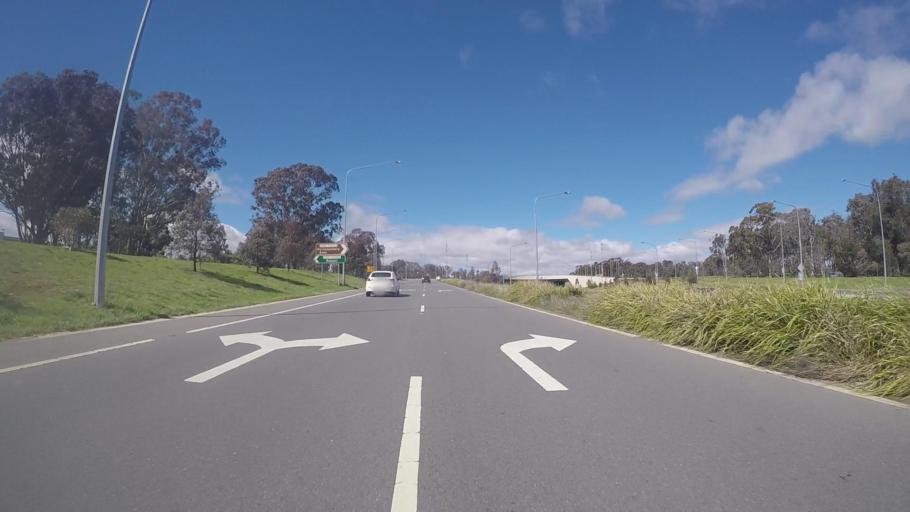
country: AU
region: Australian Capital Territory
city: Canberra
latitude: -35.2971
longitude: 149.1470
